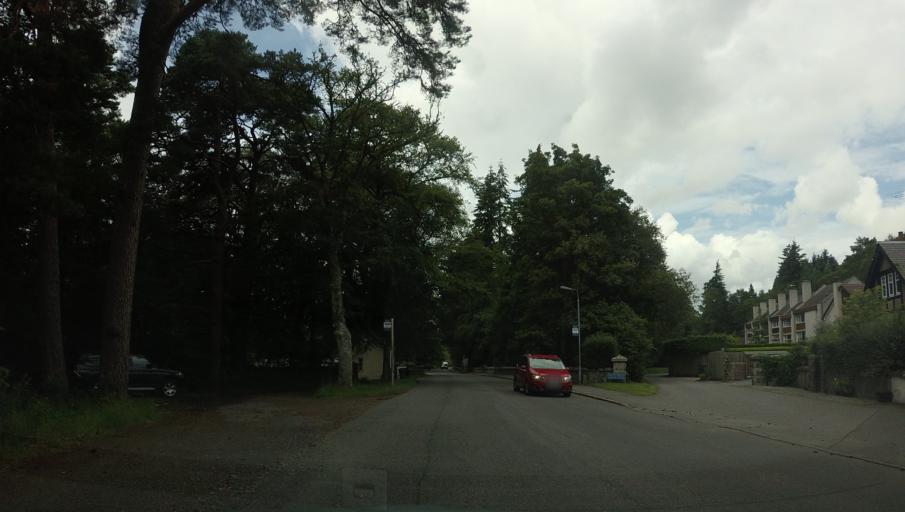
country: GB
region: Scotland
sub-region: Aberdeenshire
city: Banchory
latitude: 57.0526
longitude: -2.5128
